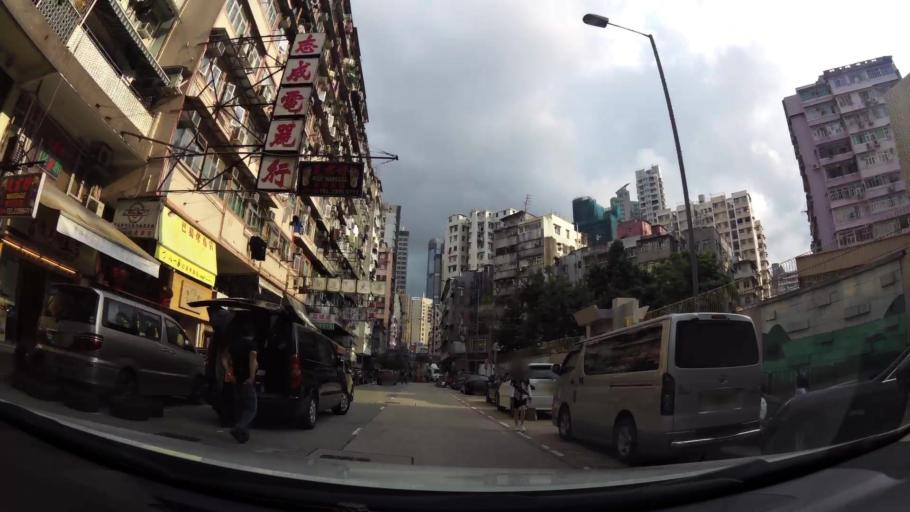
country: HK
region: Sham Shui Po
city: Sham Shui Po
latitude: 22.3262
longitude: 114.1673
